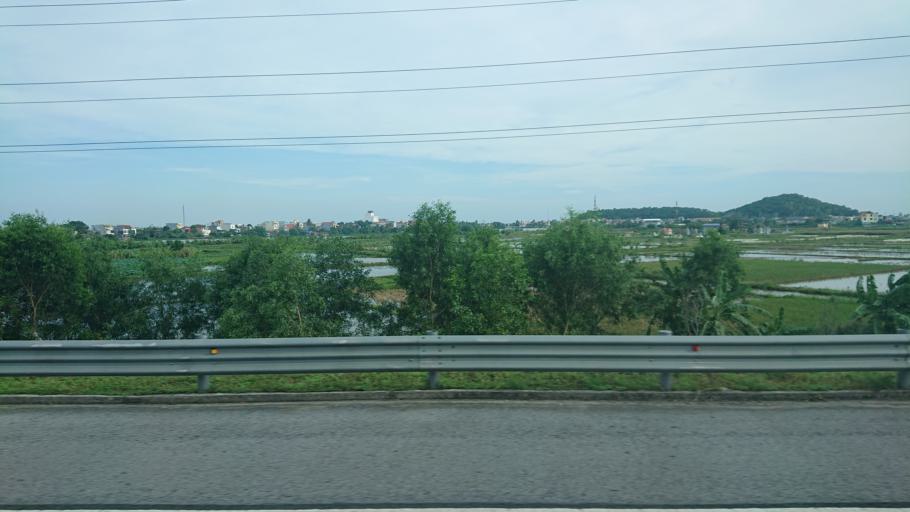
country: VN
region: Hai Phong
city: Nui Doi
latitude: 20.7654
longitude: 106.6726
